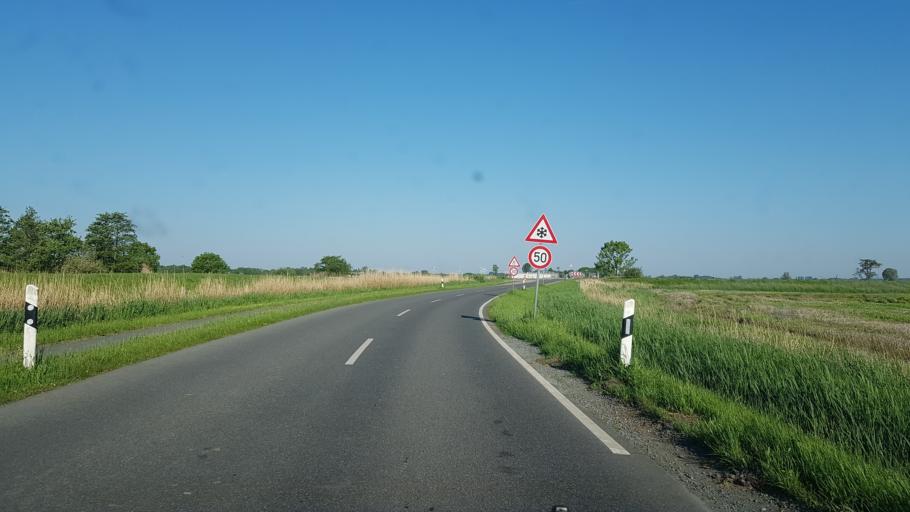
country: DE
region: Lower Saxony
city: Langen
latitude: 53.6130
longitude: 8.5607
